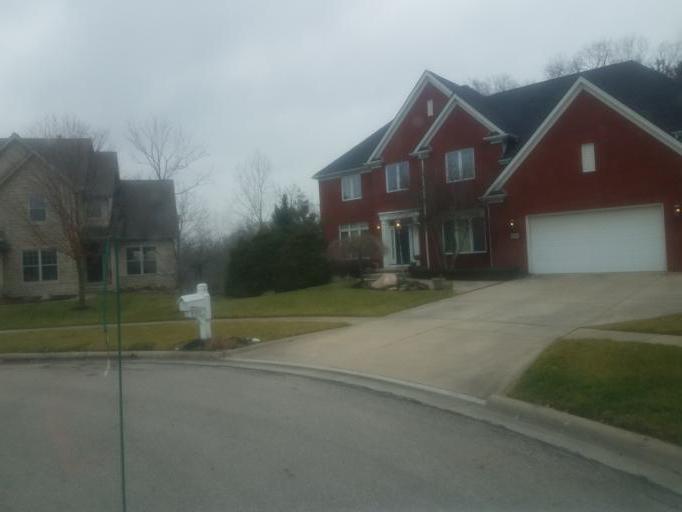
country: US
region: Ohio
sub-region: Franklin County
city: Westerville
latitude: 40.1754
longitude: -82.9403
